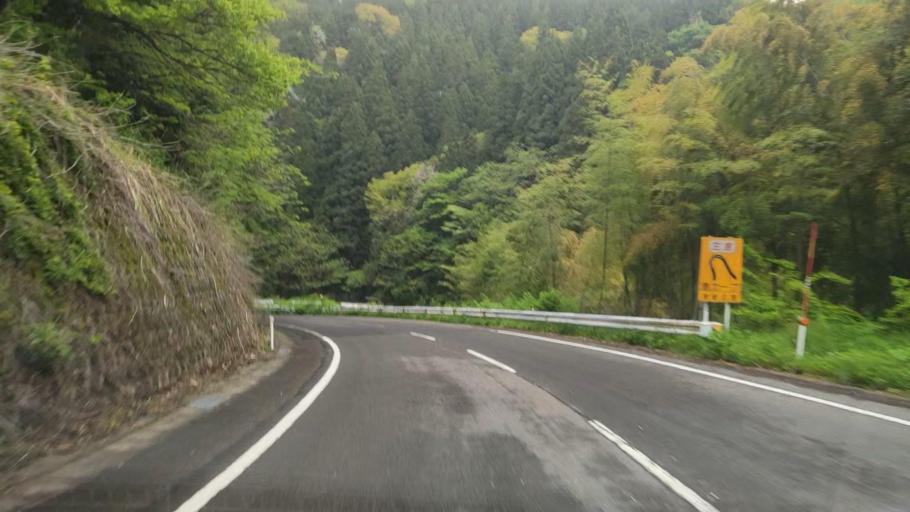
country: JP
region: Niigata
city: Gosen
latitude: 37.7153
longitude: 139.1140
